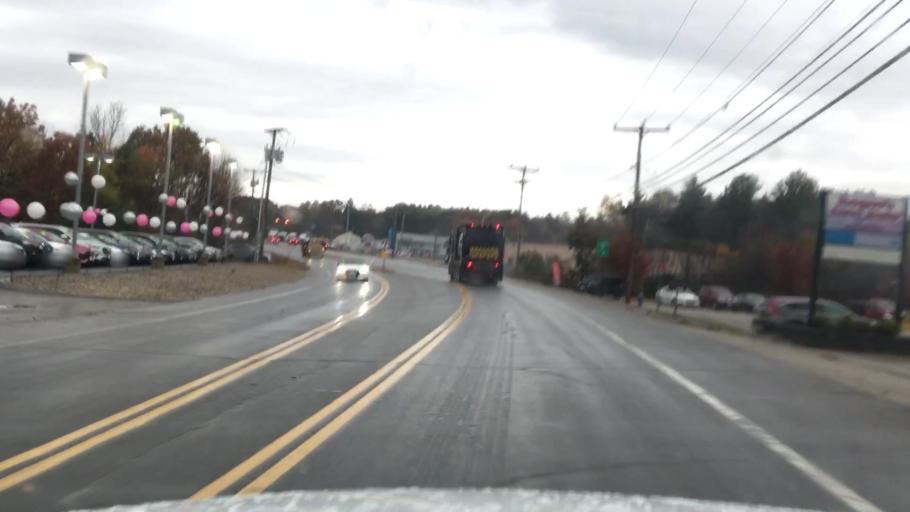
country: US
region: New Hampshire
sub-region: Strafford County
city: Somersworth
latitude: 43.2632
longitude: -70.9053
